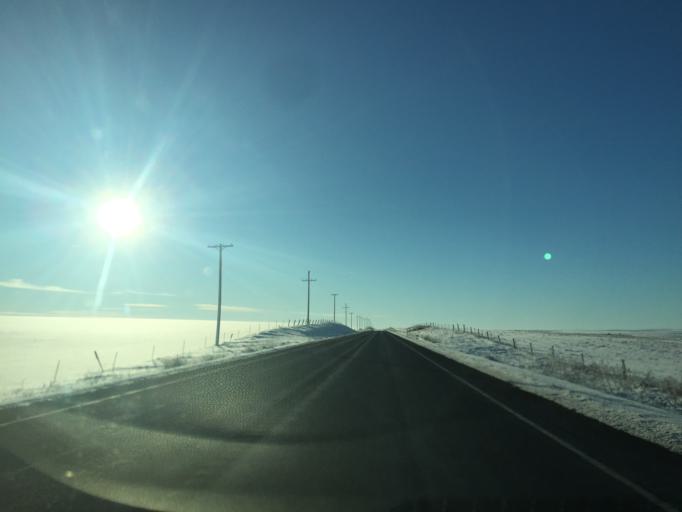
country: US
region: Washington
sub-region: Okanogan County
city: Coulee Dam
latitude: 47.7264
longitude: -118.8803
